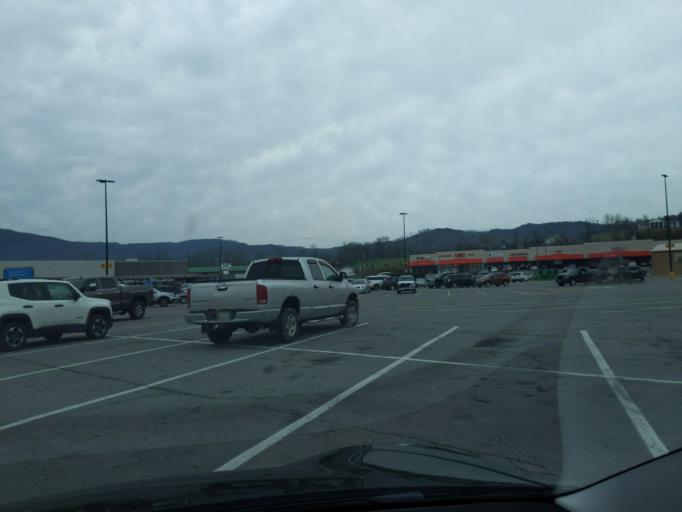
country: US
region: Kentucky
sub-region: Bell County
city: Middlesboro
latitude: 36.6219
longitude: -83.7056
